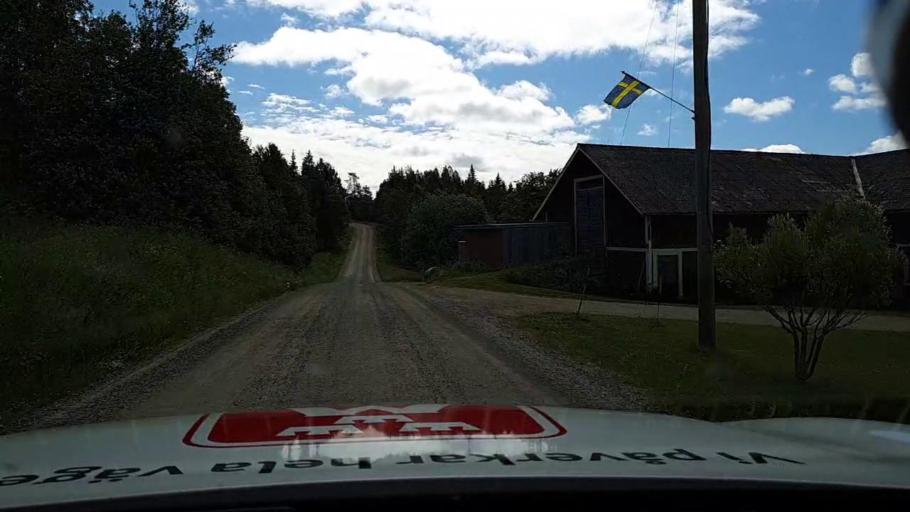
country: SE
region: Jaemtland
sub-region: Braecke Kommun
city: Braecke
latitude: 62.7709
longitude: 15.4846
